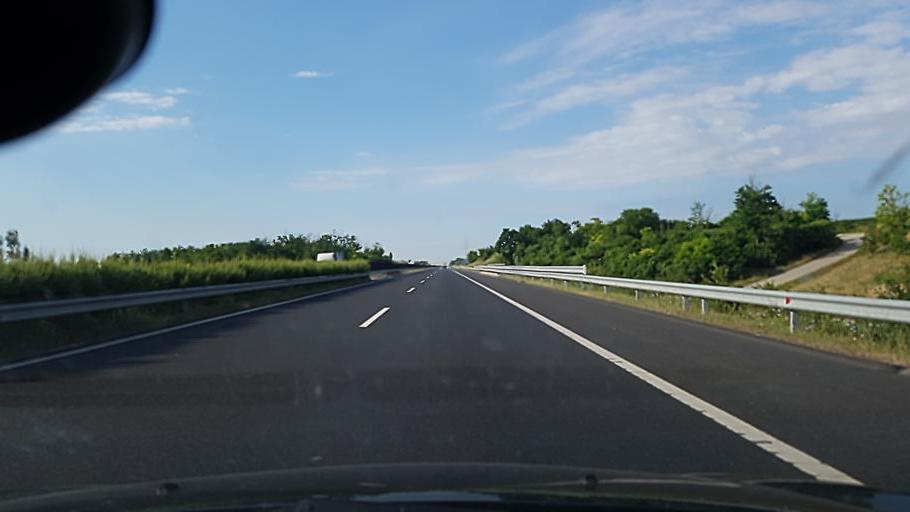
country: HU
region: Fejer
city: Rackeresztur
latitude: 47.2179
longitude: 18.8191
